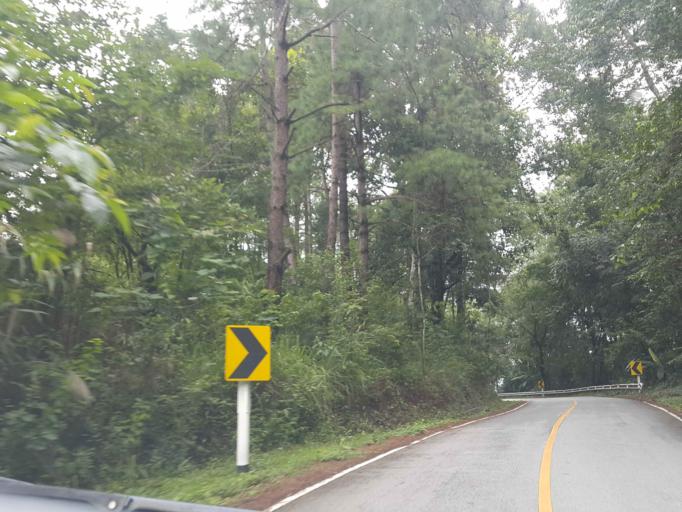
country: TH
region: Chiang Mai
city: Mae Chaem
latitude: 18.5111
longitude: 98.4742
